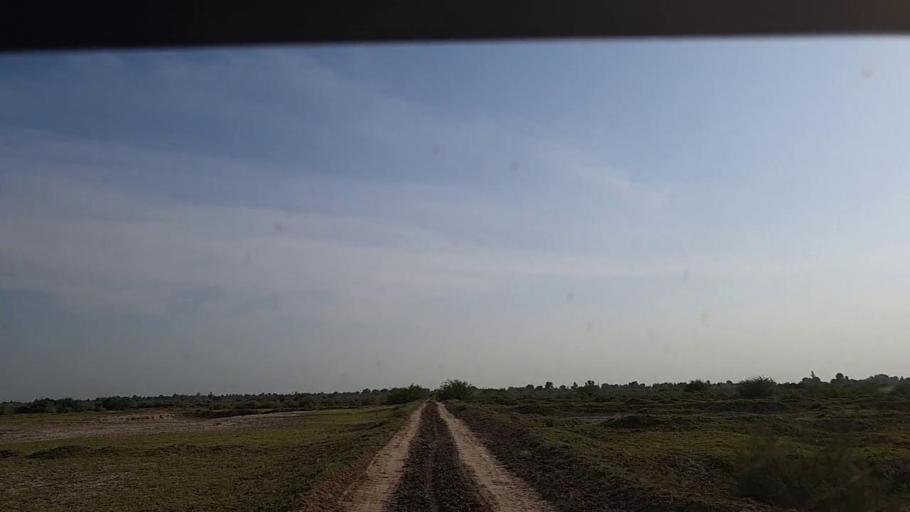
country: PK
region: Sindh
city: Adilpur
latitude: 27.9073
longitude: 69.2117
